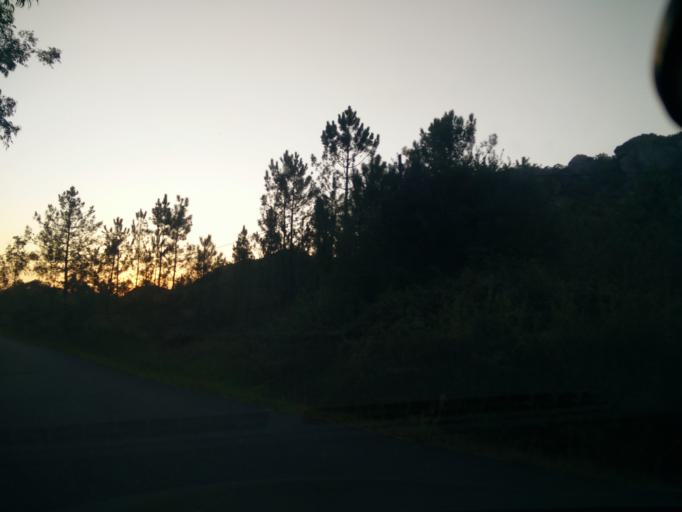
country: ES
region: Galicia
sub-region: Provincia da Coruna
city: Monfero
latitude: 43.3550
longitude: -8.0487
